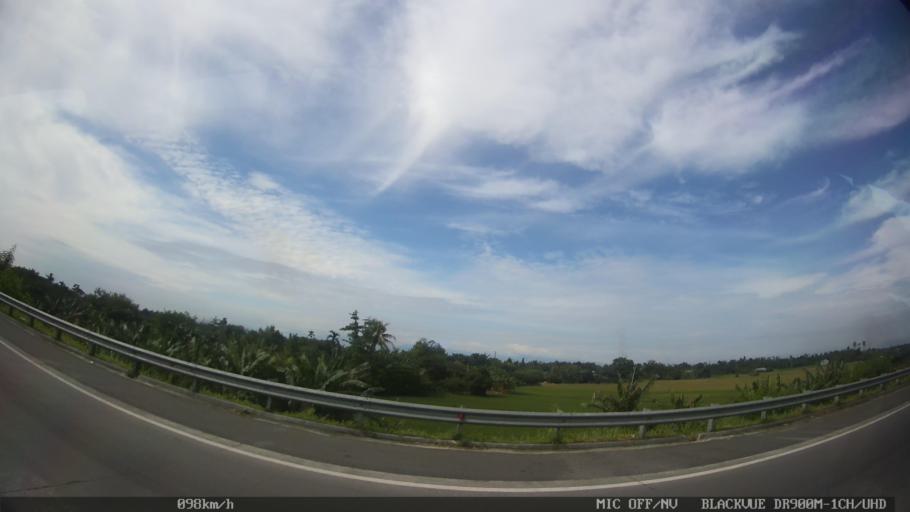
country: ID
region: North Sumatra
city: Sunggal
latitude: 3.6394
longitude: 98.5720
